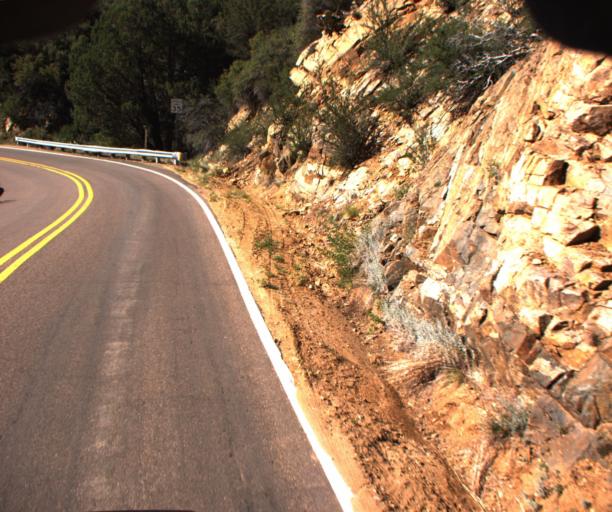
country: US
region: Arizona
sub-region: Yavapai County
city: Prescott
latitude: 34.4660
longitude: -112.5206
